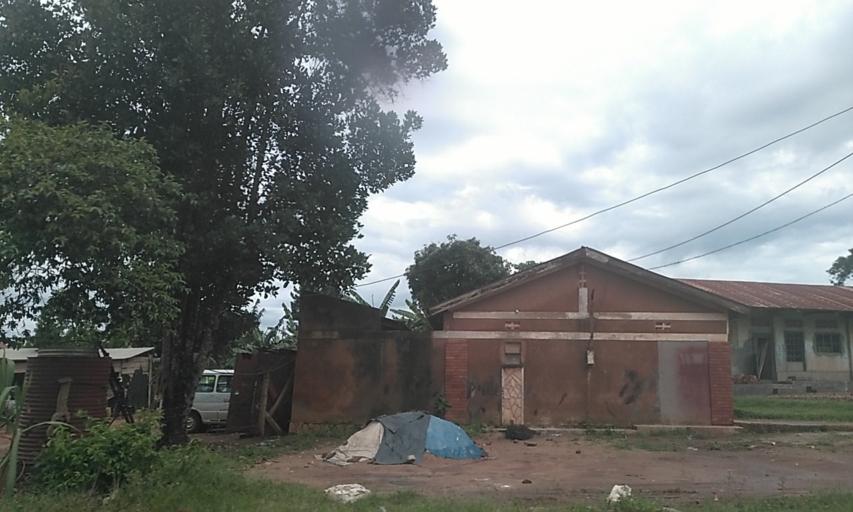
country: UG
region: Central Region
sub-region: Wakiso District
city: Bweyogerere
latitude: 0.3962
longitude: 32.6989
